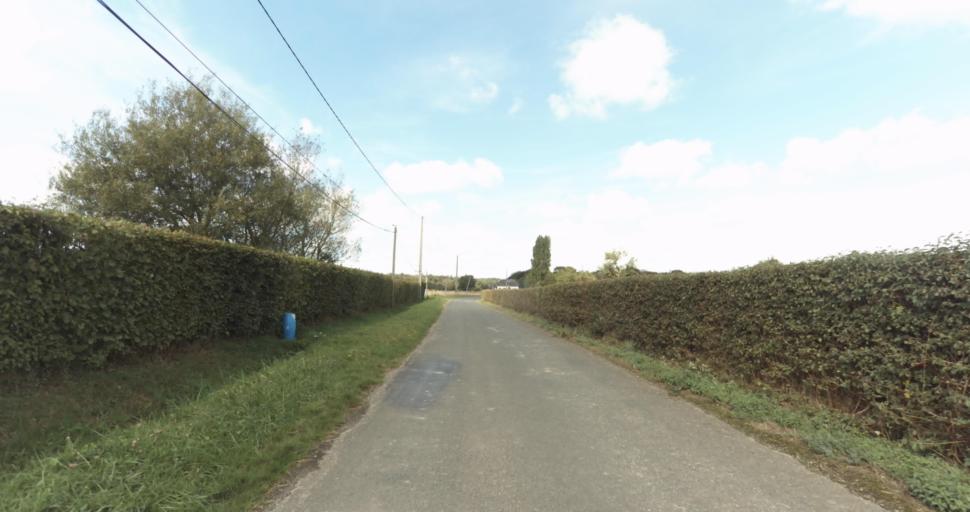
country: FR
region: Lower Normandy
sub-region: Departement du Calvados
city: Orbec
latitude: 48.9432
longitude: 0.3783
